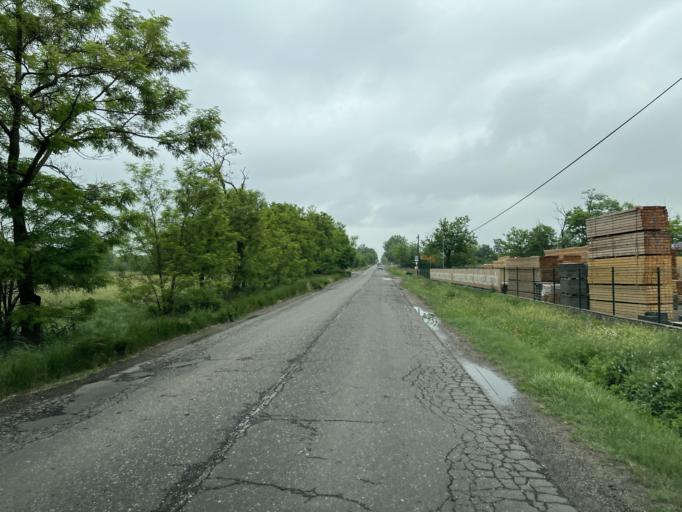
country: HU
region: Pest
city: Tura
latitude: 47.6181
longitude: 19.6107
